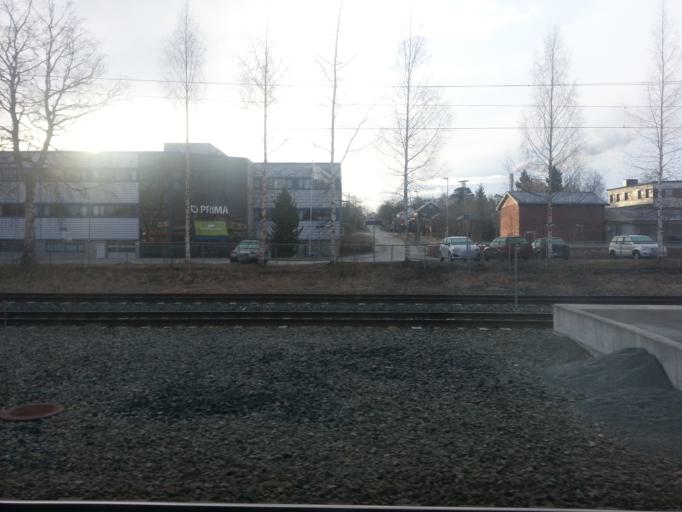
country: NO
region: Sor-Trondelag
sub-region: Trondheim
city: Trondheim
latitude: 63.3513
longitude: 10.3579
